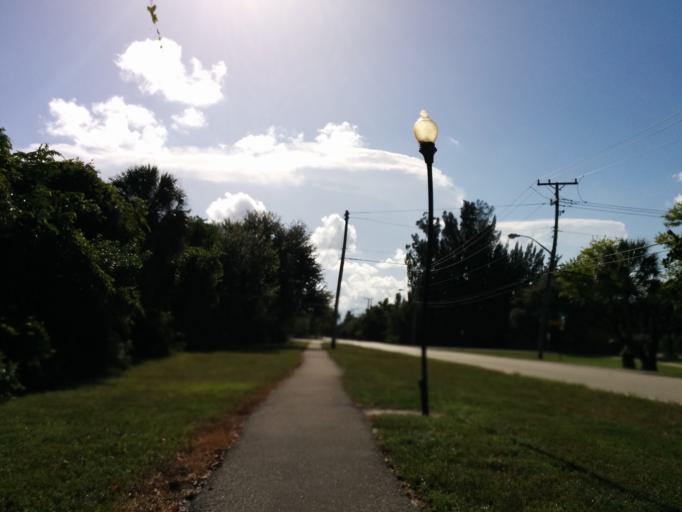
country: US
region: Florida
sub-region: Broward County
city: Davie
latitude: 26.0655
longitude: -80.2364
